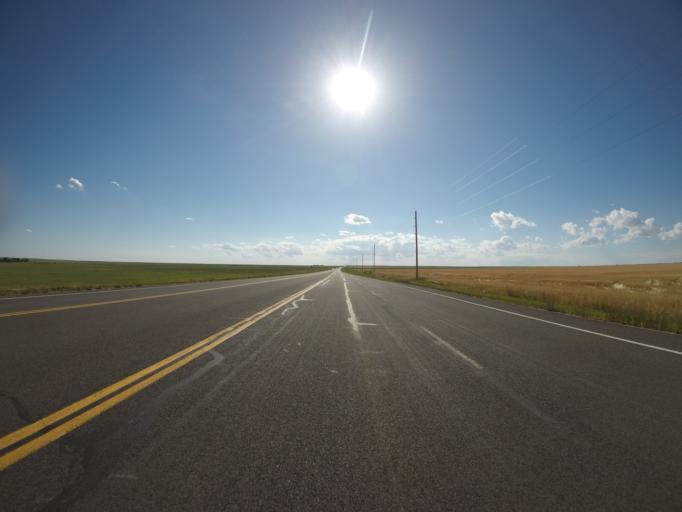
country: US
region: Colorado
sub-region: Morgan County
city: Brush
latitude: 40.6099
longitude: -103.6810
